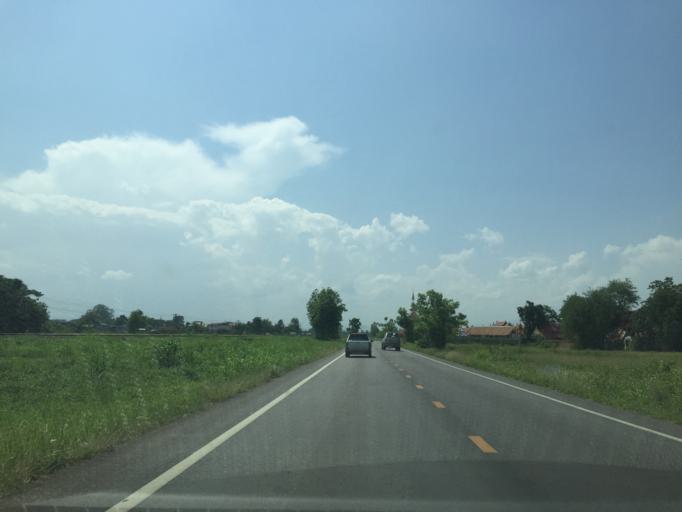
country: TH
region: Lamphun
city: Lamphun
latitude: 18.5716
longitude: 99.0306
